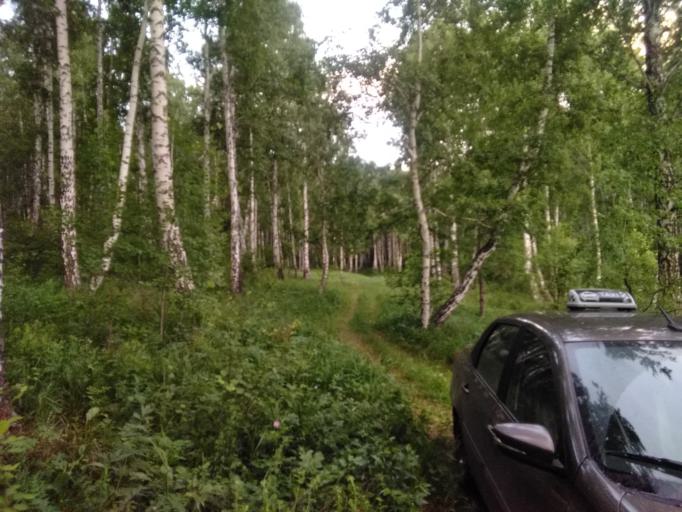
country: RU
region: Bashkortostan
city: Uchaly
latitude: 54.3368
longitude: 59.3382
